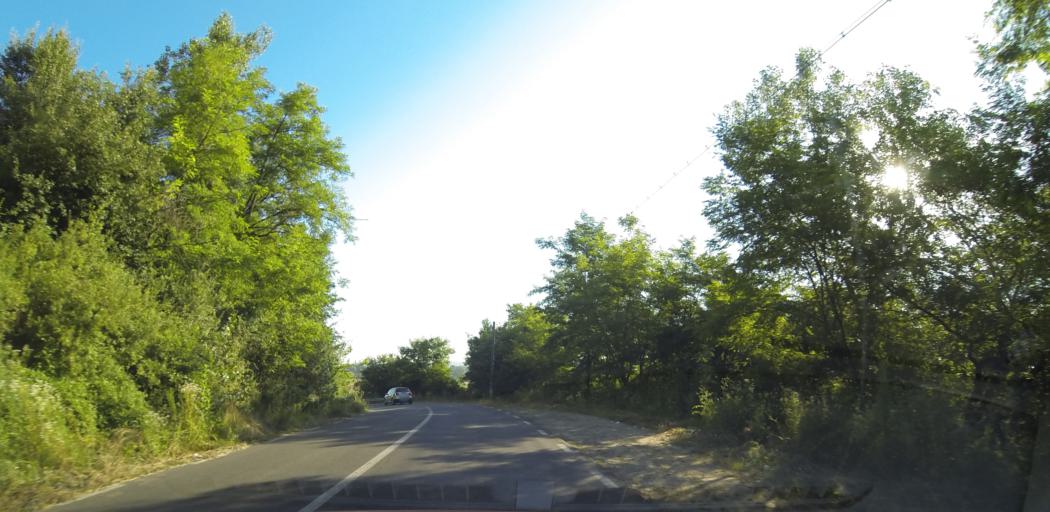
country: RO
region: Valcea
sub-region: Comuna Lacusteni
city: Lacusteni
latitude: 44.7177
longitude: 23.9025
